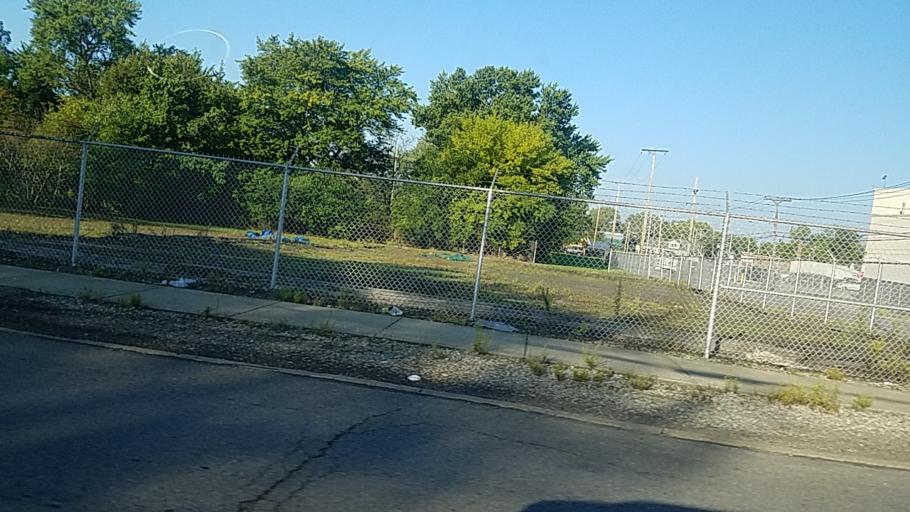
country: US
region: Ohio
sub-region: Trumbull County
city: Niles
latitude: 41.1751
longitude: -80.7514
